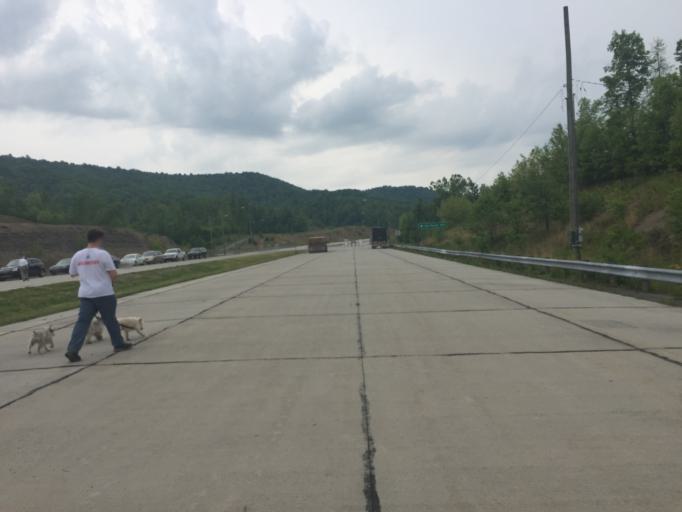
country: US
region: West Virginia
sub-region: Randolph County
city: Elkins
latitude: 39.0121
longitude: -79.8110
